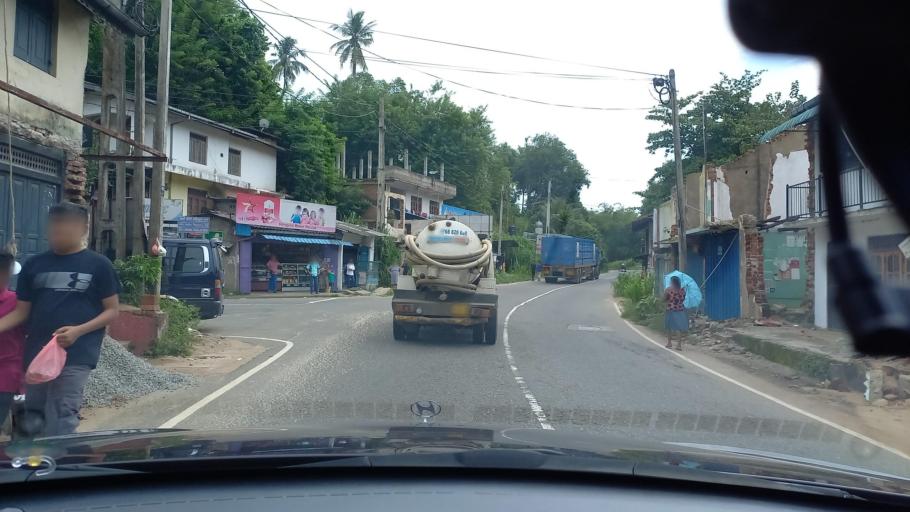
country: LK
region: Central
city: Kadugannawa
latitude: 7.2476
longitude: 80.4686
